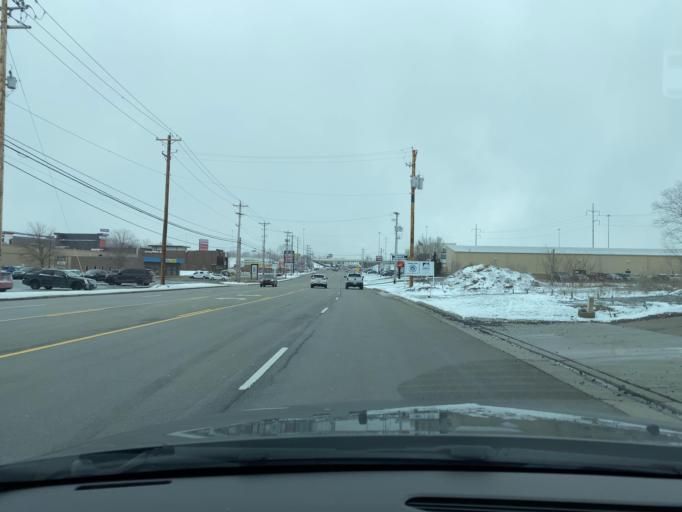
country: US
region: Ohio
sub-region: Stark County
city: North Canton
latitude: 40.8630
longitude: -81.4227
